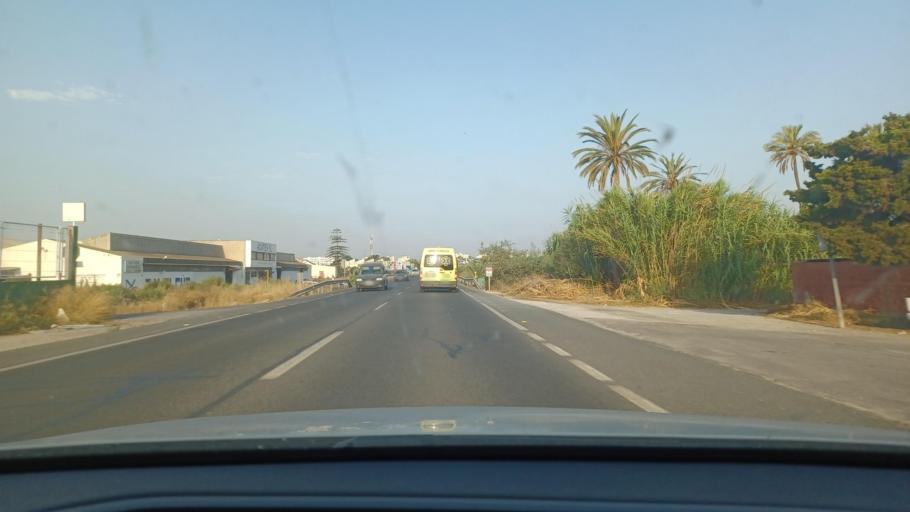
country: ES
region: Valencia
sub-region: Provincia de Alicante
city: Elche
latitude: 38.2760
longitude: -0.6568
